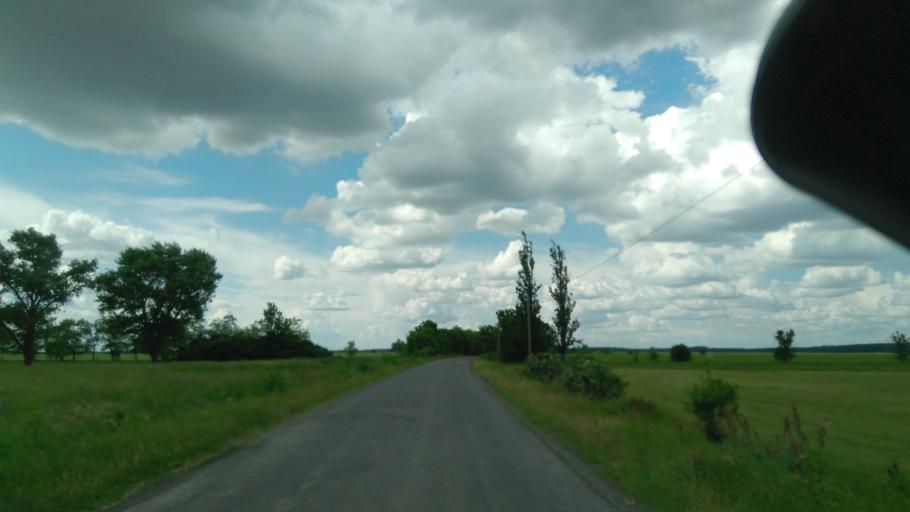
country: HU
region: Bekes
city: Bucsa
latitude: 47.1217
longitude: 21.0865
